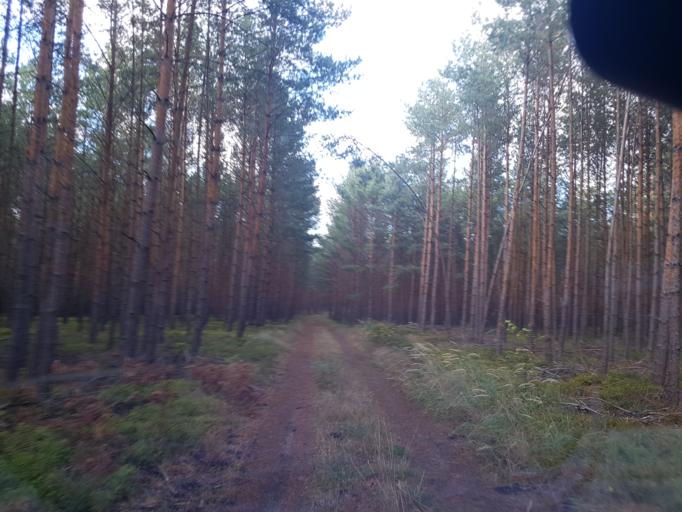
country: DE
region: Brandenburg
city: Finsterwalde
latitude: 51.5577
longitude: 13.6983
